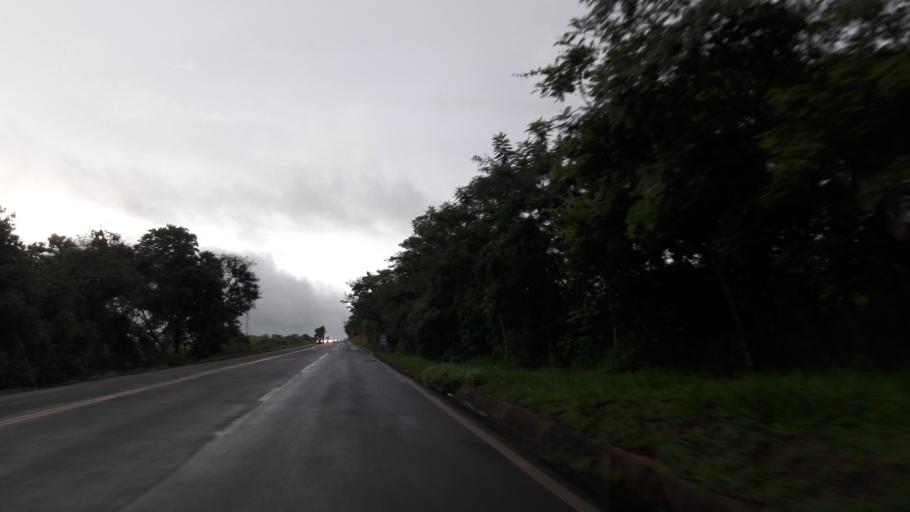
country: BR
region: Parana
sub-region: Assai
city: Assai
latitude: -23.2479
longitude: -50.7339
